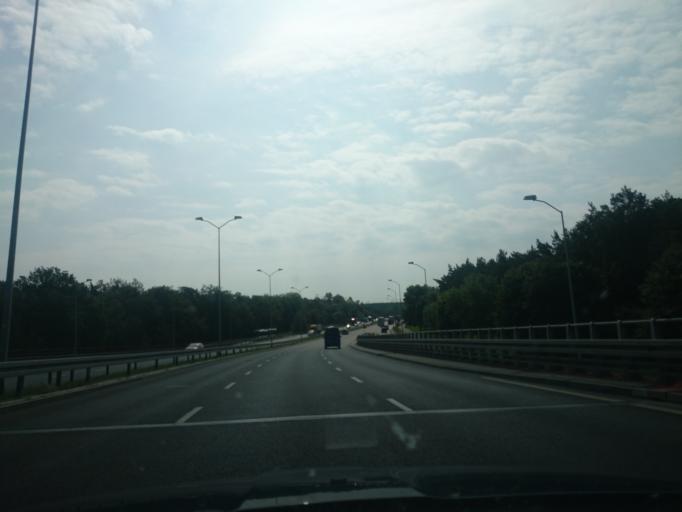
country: PL
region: West Pomeranian Voivodeship
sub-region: Powiat gryfinski
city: Stare Czarnowo
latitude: 53.3811
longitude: 14.6844
